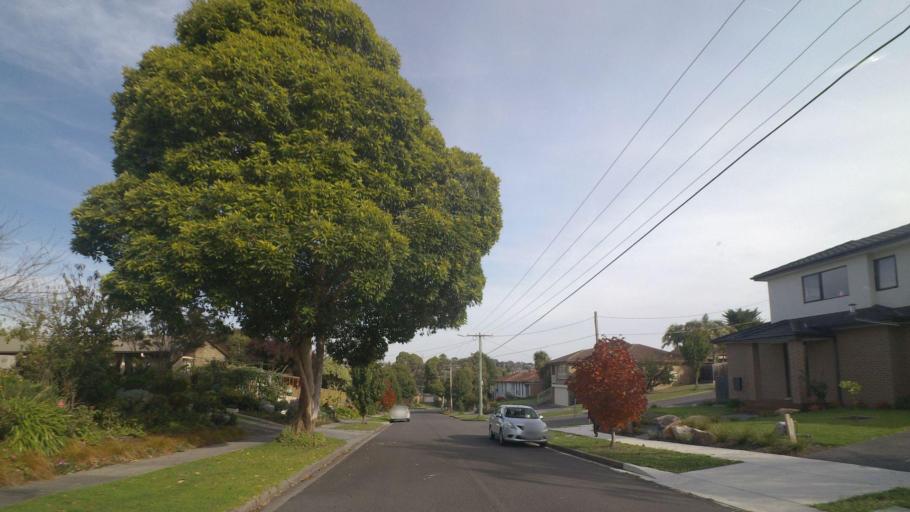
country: AU
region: Victoria
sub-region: Manningham
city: Doncaster East
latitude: -37.7783
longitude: 145.1517
